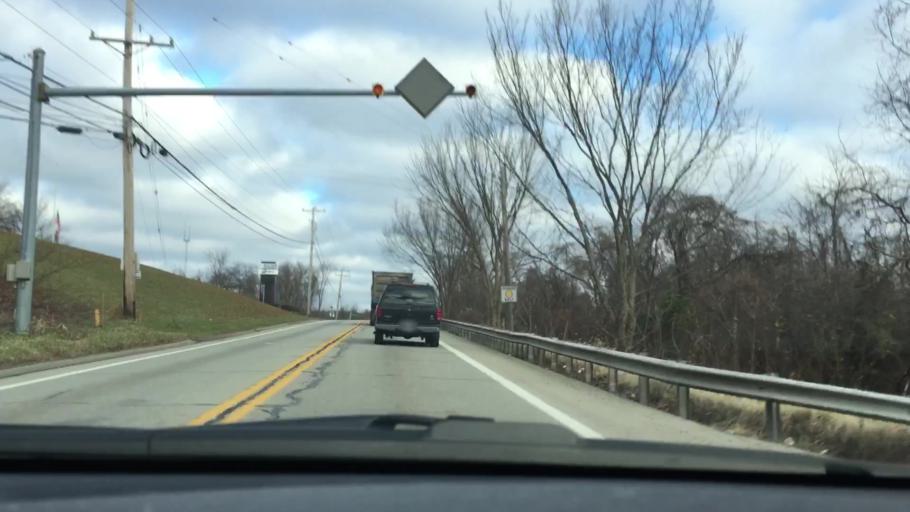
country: US
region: Pennsylvania
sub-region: Westmoreland County
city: Trafford
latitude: 40.3768
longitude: -79.7769
